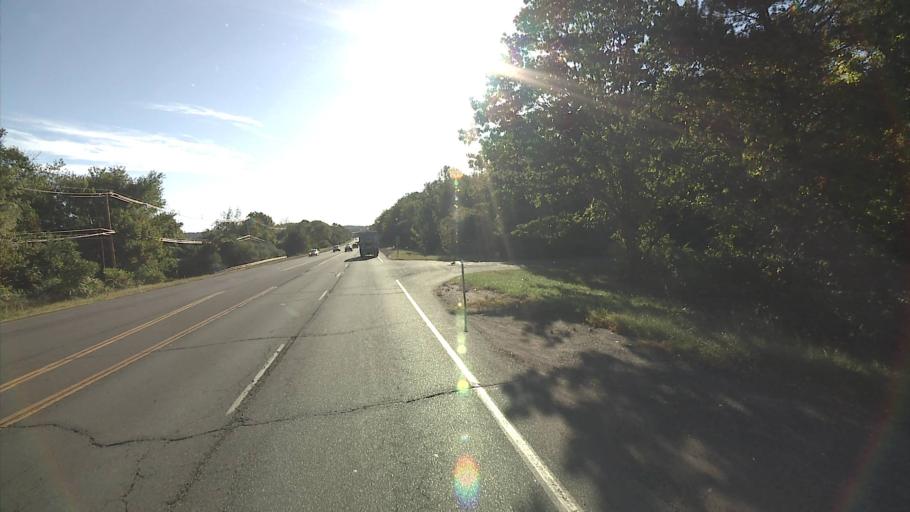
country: US
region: Connecticut
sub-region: New Haven County
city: Wallingford
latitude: 41.4832
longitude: -72.7841
